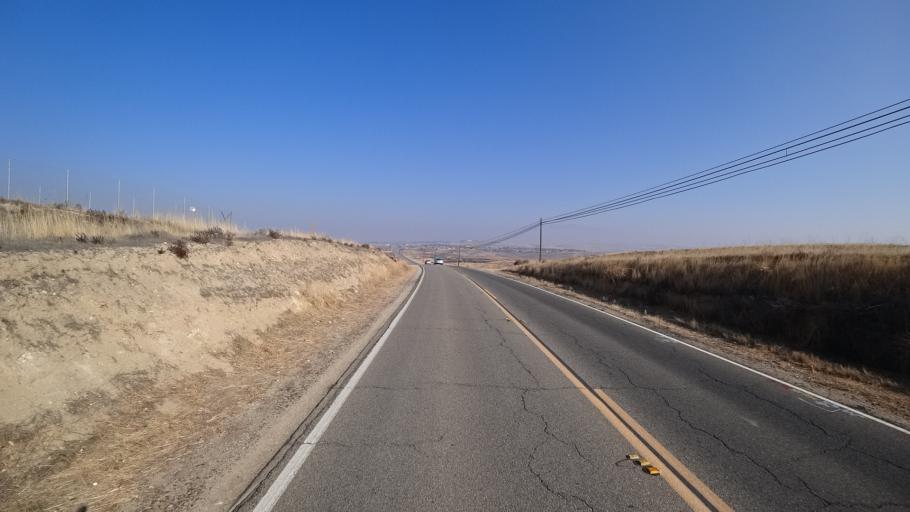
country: US
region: California
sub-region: Kern County
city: Bakersfield
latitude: 35.3833
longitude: -118.8983
